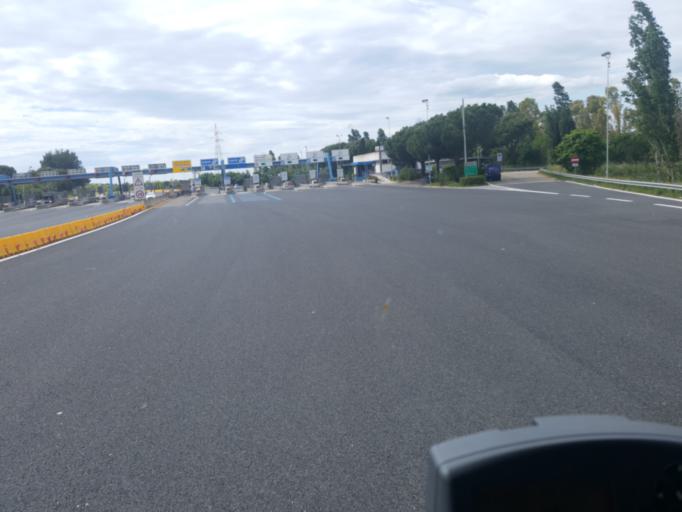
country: IT
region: Latium
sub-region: Citta metropolitana di Roma Capitale
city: Ara Nova
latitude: 41.9152
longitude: 12.2126
